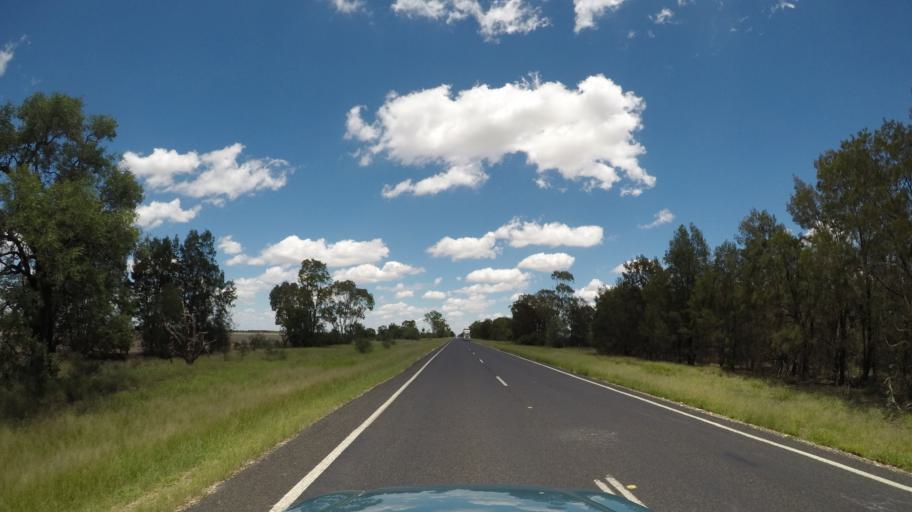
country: AU
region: Queensland
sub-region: Goondiwindi
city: Goondiwindi
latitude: -28.1646
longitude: 150.5361
